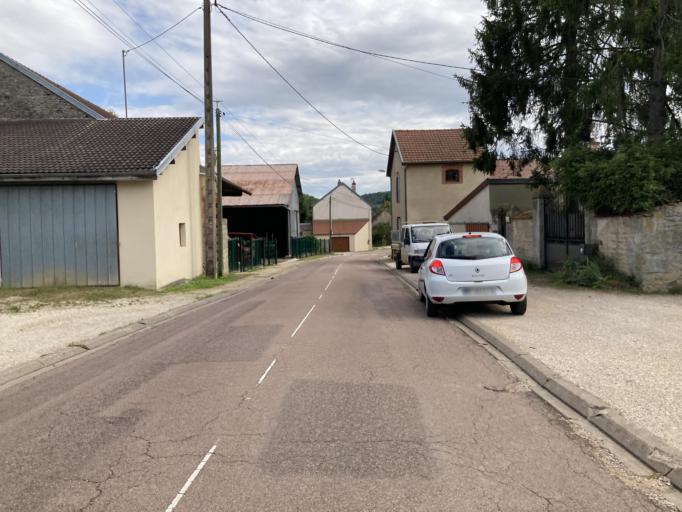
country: FR
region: Bourgogne
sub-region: Departement de la Cote-d'Or
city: Montbard
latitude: 47.6245
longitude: 4.3688
